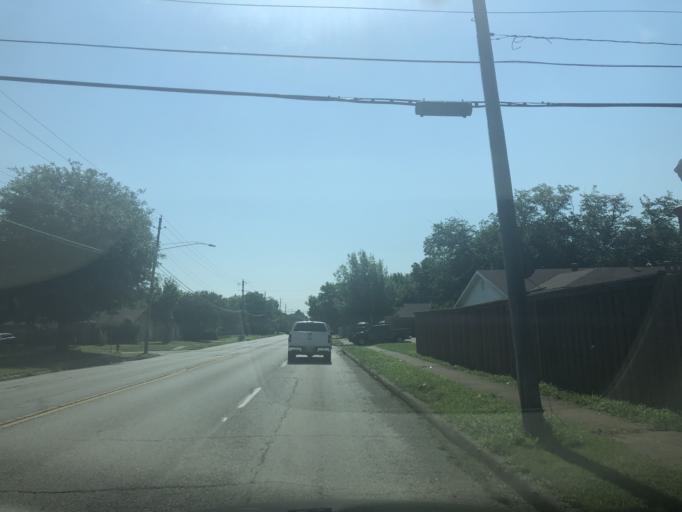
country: US
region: Texas
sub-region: Dallas County
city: Grand Prairie
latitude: 32.7204
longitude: -97.0117
